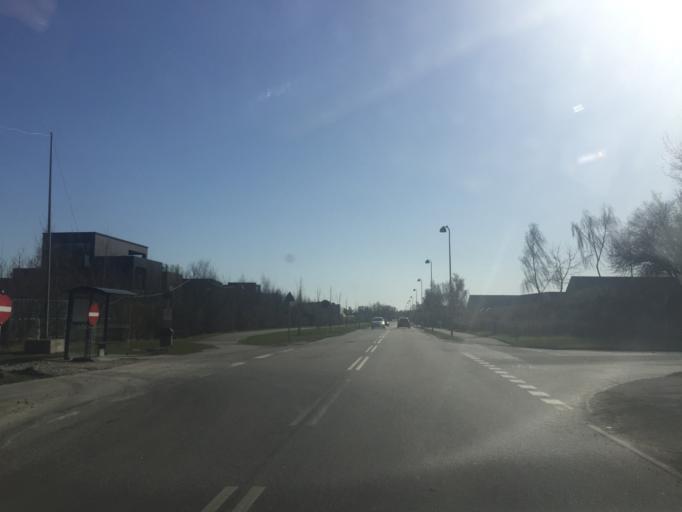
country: DK
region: Capital Region
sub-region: Glostrup Kommune
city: Glostrup
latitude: 55.6854
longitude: 12.4207
